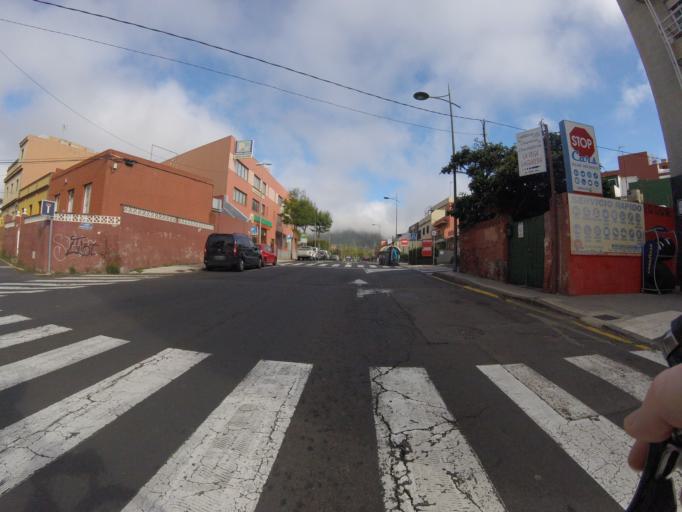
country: ES
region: Canary Islands
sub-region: Provincia de Santa Cruz de Tenerife
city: La Laguna
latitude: 28.4890
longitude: -16.3267
